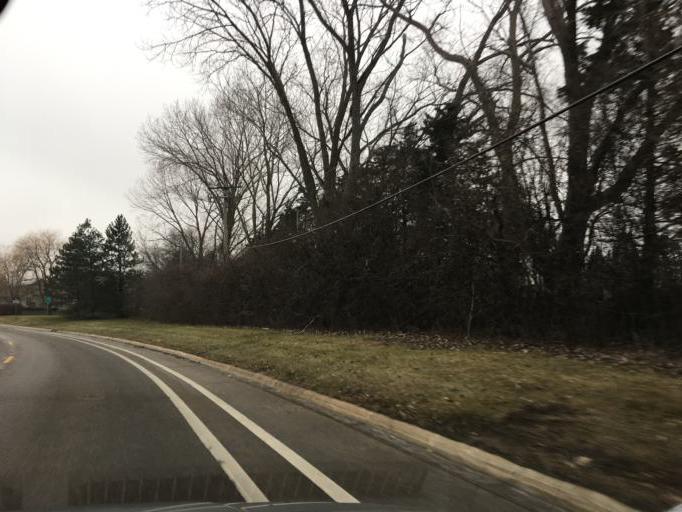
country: US
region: Illinois
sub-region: McHenry County
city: Lakewood
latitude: 42.2190
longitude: -88.3489
